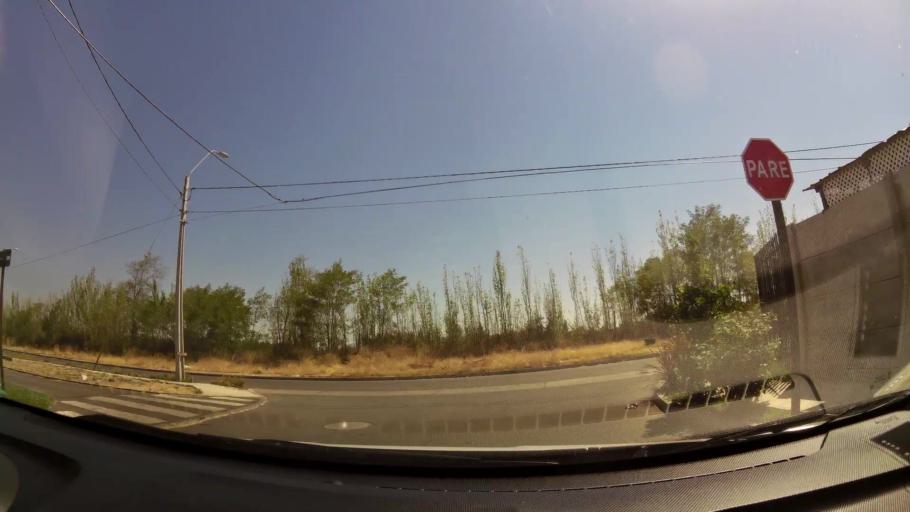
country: CL
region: Maule
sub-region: Provincia de Curico
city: Curico
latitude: -34.9607
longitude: -71.2309
